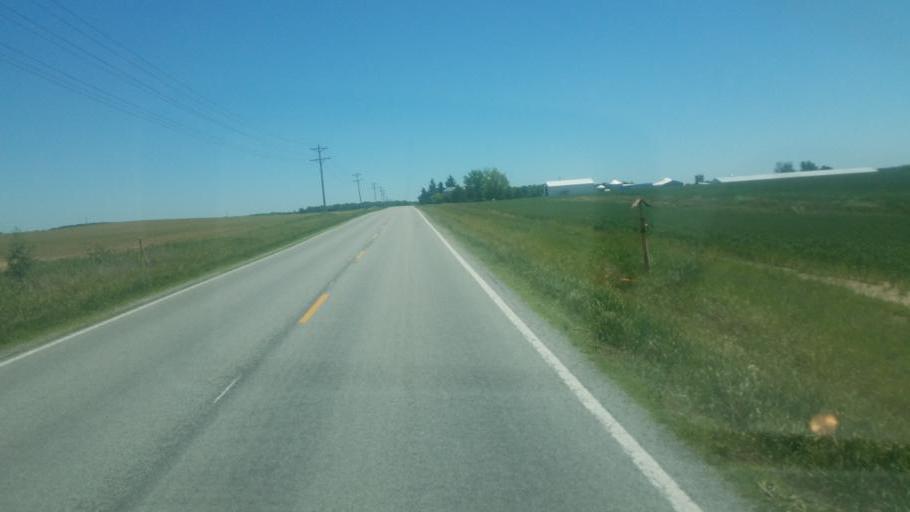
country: US
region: Ohio
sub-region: Miami County
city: Piqua
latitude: 40.2202
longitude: -84.3128
